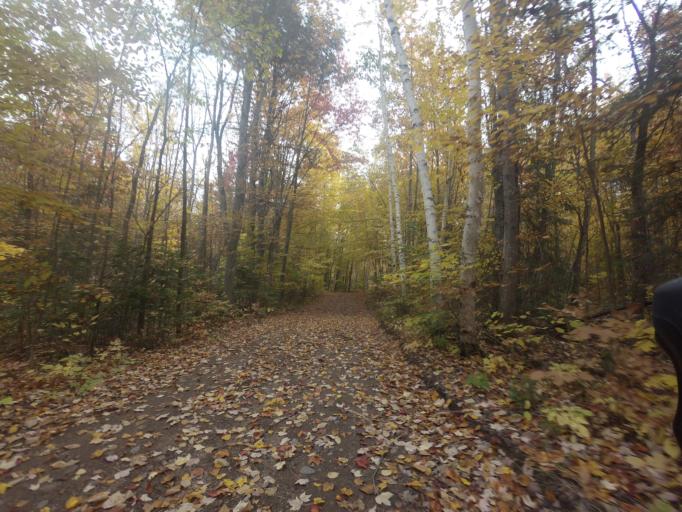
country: CA
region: Ontario
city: Pembroke
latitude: 45.7268
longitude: -77.2262
